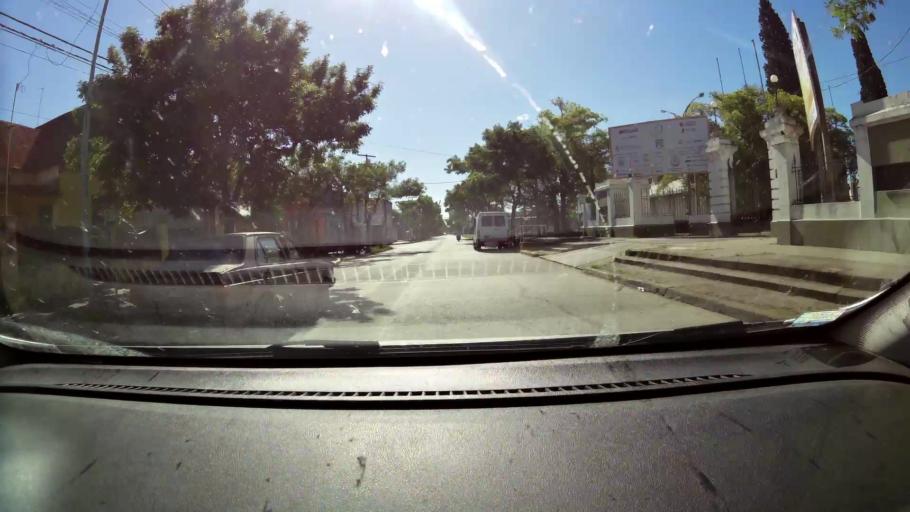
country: AR
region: Santa Fe
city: Rafaela
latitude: -31.2442
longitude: -61.4846
